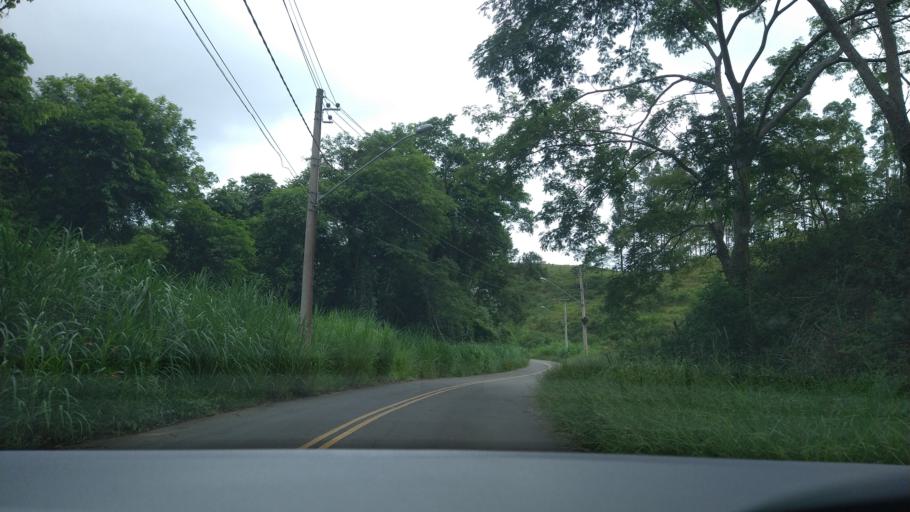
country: BR
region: Minas Gerais
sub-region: Vicosa
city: Vicosa
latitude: -20.7760
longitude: -42.8626
